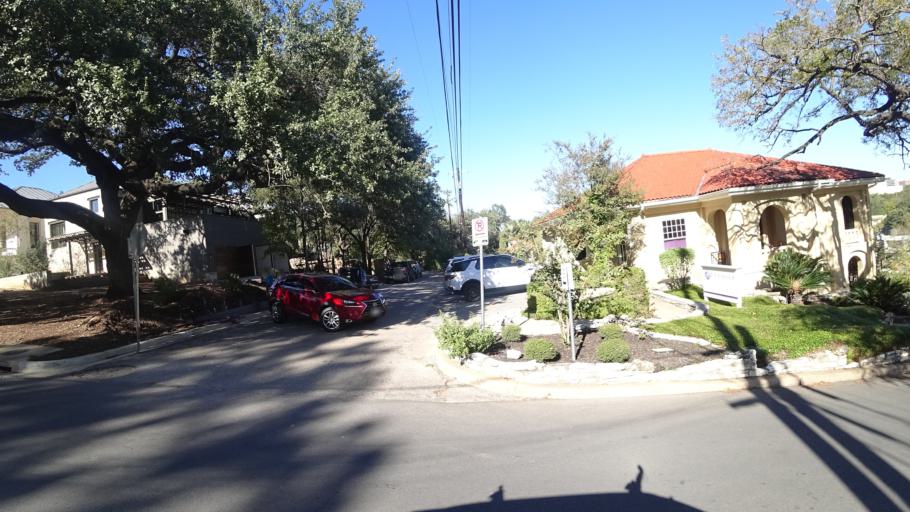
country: US
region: Texas
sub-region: Travis County
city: Austin
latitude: 30.2742
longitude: -97.7537
